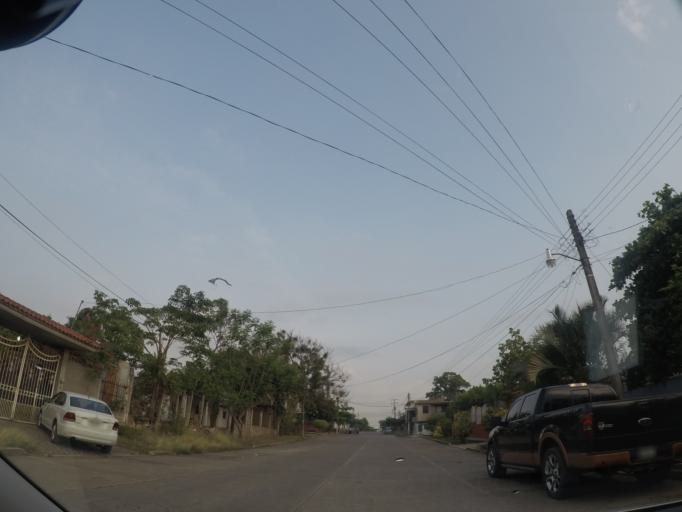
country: MX
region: Oaxaca
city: Matias Romero
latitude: 16.8727
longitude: -95.0398
